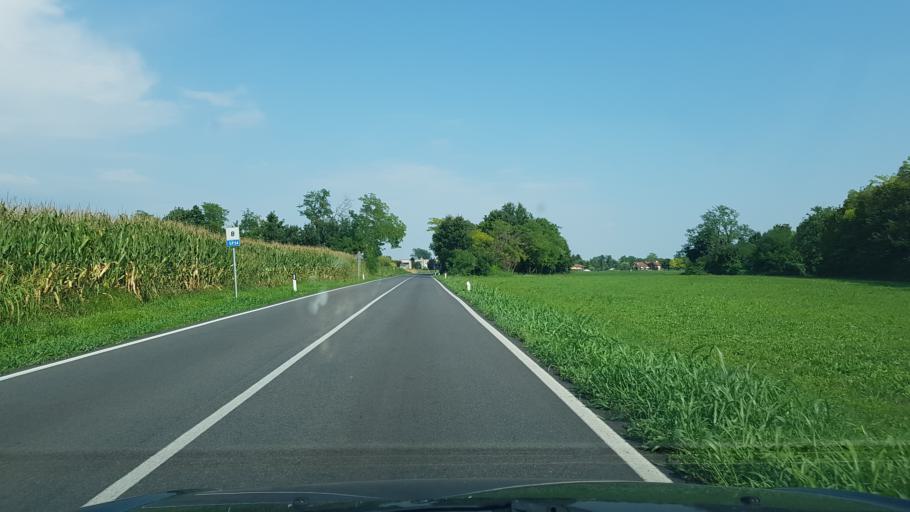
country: IT
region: Friuli Venezia Giulia
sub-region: Provincia di Pordenone
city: San Quirino
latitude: 46.0535
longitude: 12.6522
